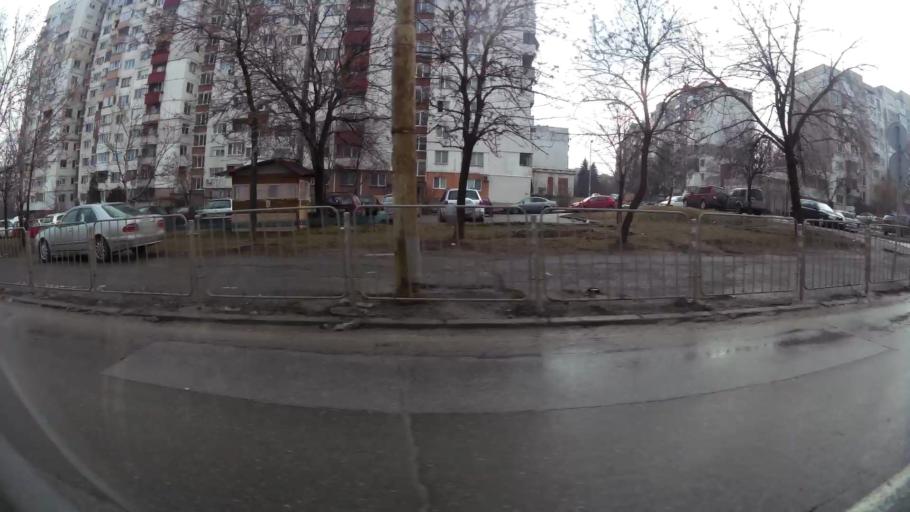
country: BG
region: Sofiya
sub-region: Obshtina Bozhurishte
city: Bozhurishte
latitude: 42.7246
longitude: 23.2436
